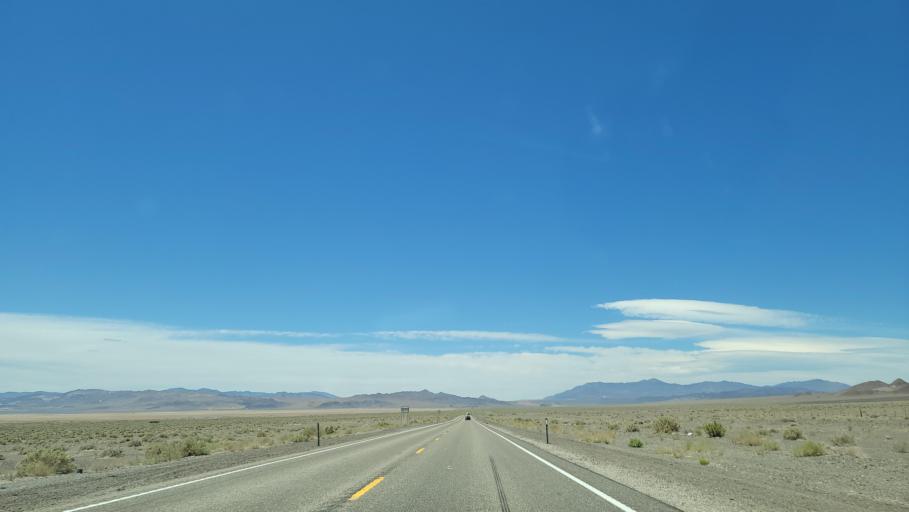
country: US
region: Nevada
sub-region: Nye County
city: Tonopah
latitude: 38.0375
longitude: -117.8907
